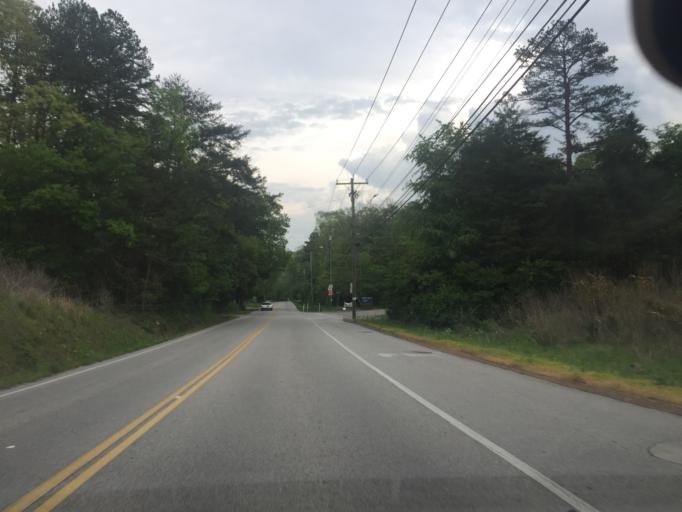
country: US
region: Tennessee
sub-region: Hamilton County
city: Harrison
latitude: 35.1216
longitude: -85.0938
